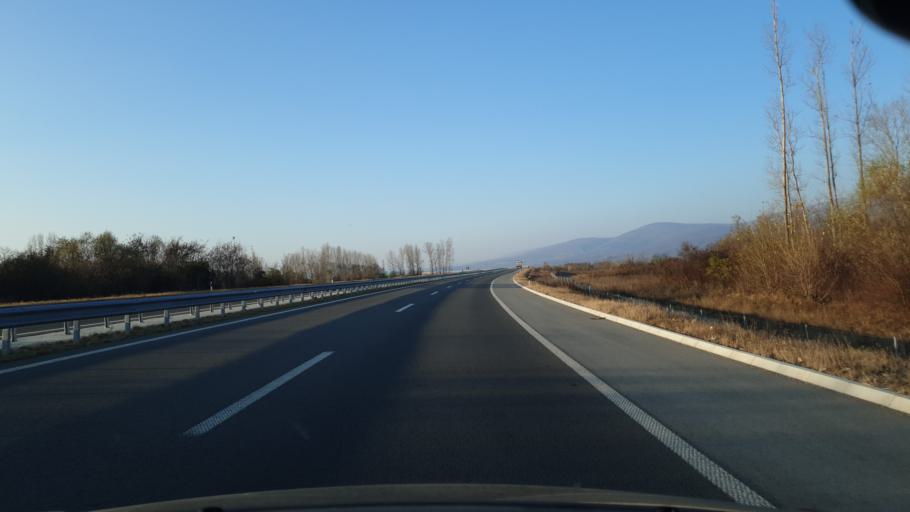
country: RS
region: Central Serbia
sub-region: Pirotski Okrug
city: Dimitrovgrad
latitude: 43.0644
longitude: 22.6804
